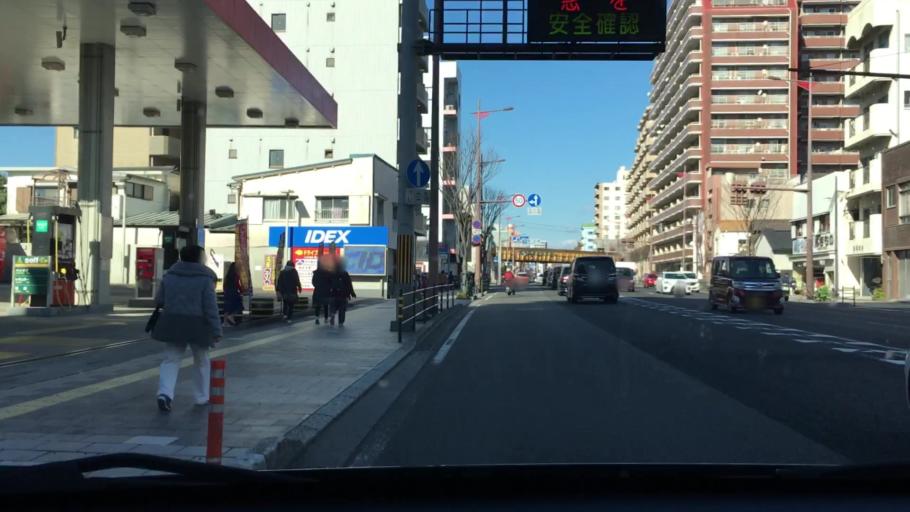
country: JP
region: Kagoshima
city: Kagoshima-shi
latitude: 31.5915
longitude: 130.5450
